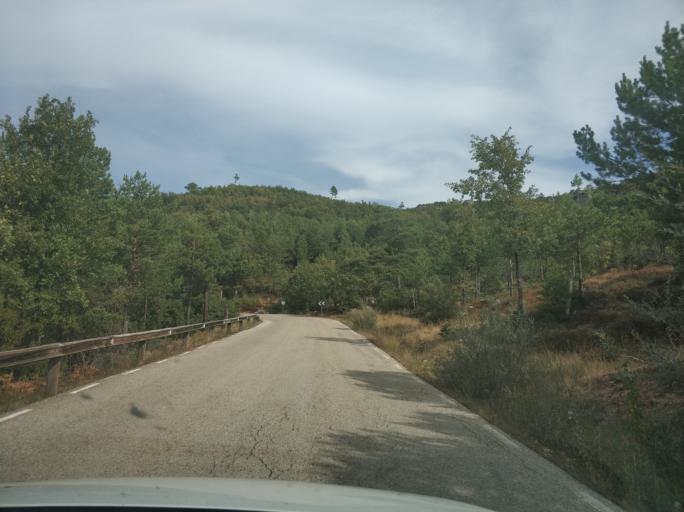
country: ES
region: Castille and Leon
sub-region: Provincia de Soria
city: Duruelo de la Sierra
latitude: 41.9060
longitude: -2.9420
